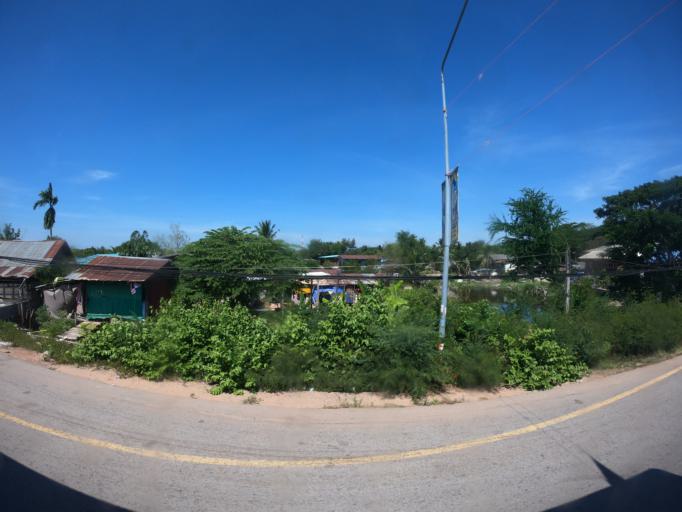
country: TH
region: Khon Kaen
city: Ban Phai
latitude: 16.0570
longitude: 102.7218
